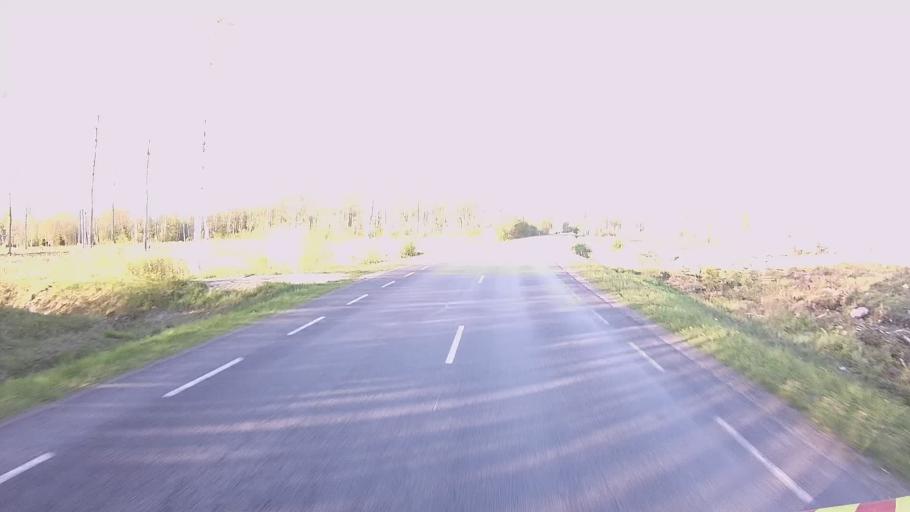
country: EE
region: Viljandimaa
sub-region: Viiratsi vald
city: Viiratsi
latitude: 58.4652
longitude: 25.7549
